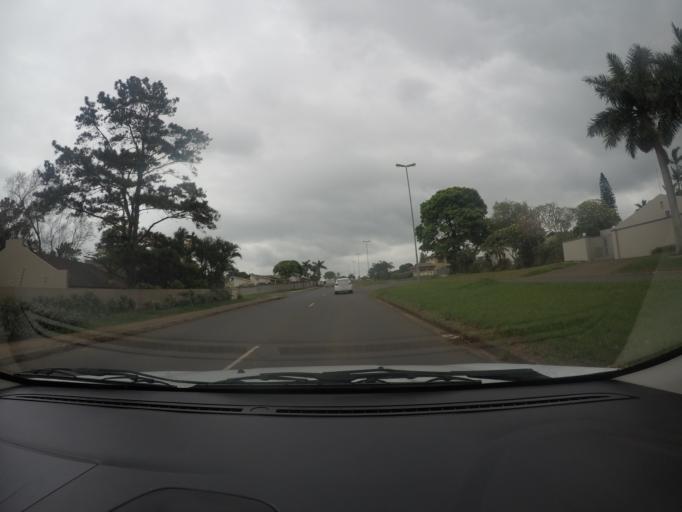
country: ZA
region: KwaZulu-Natal
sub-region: uThungulu District Municipality
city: Empangeni
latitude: -28.7628
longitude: 31.8963
